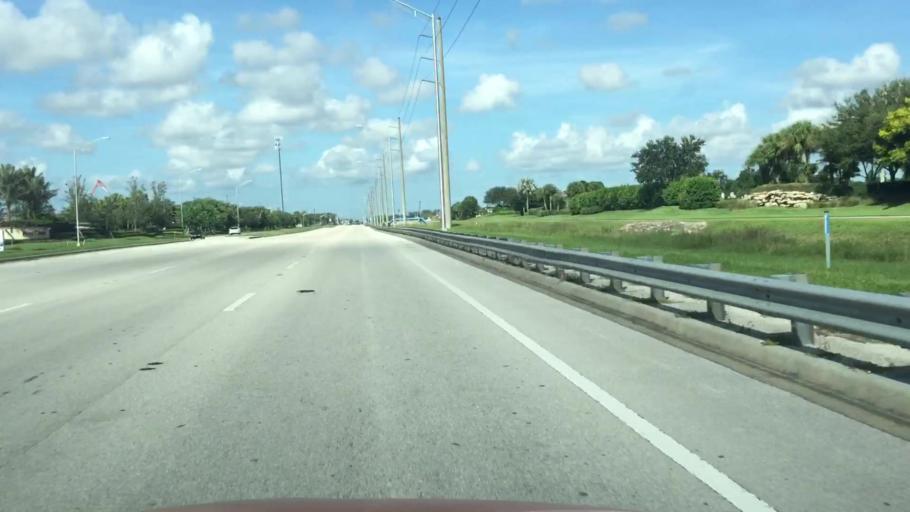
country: US
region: Florida
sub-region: Collier County
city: Vineyards
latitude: 26.2732
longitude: -81.6762
